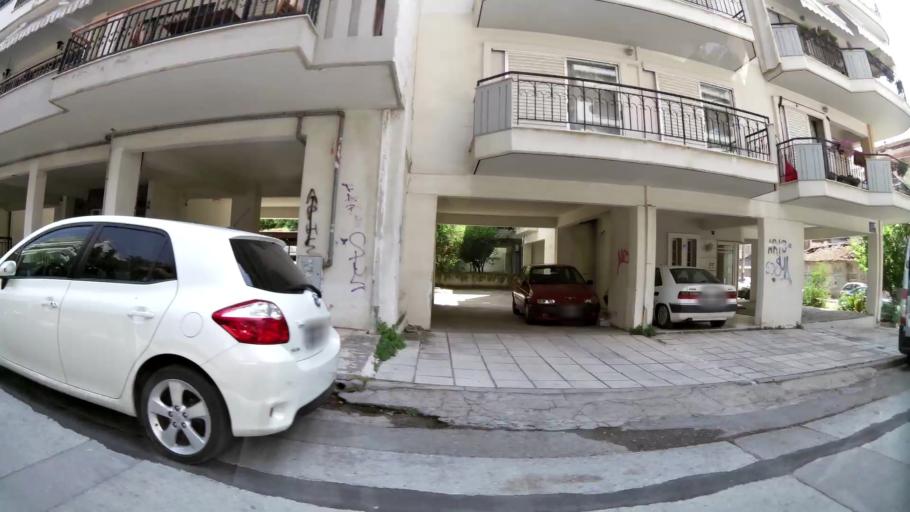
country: GR
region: Central Macedonia
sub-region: Nomos Thessalonikis
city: Evosmos
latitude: 40.6719
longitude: 22.9071
